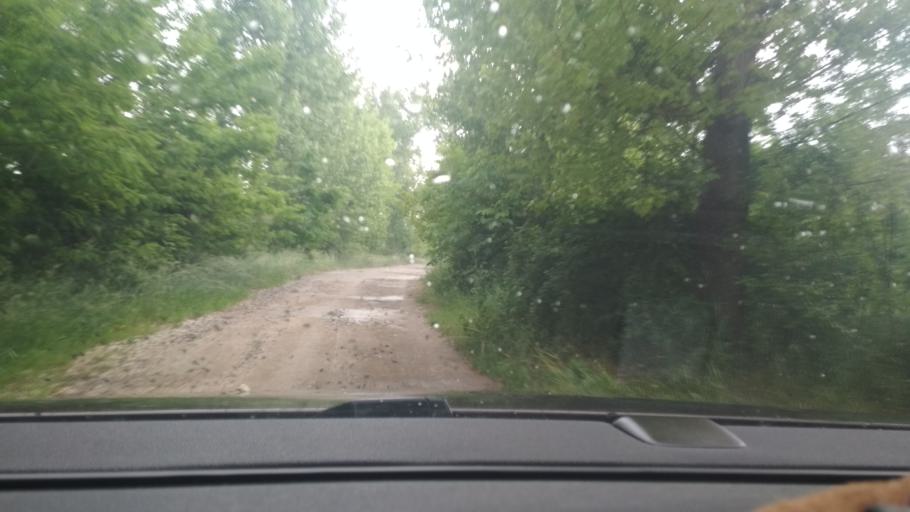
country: MD
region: Singerei
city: Biruinta
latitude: 47.7480
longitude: 28.1397
